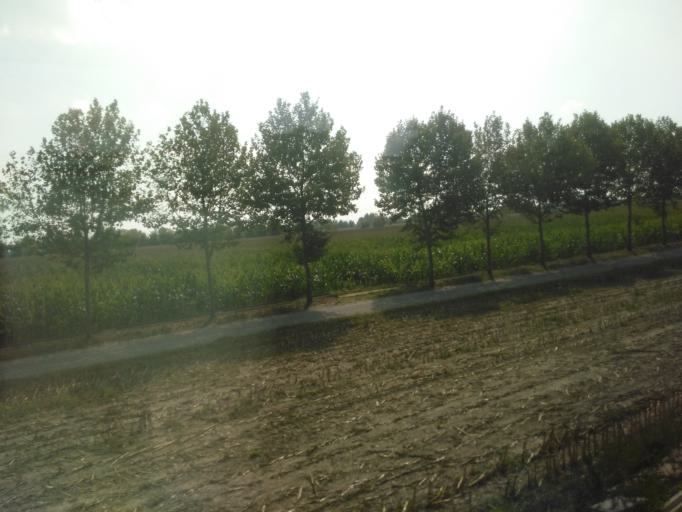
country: IT
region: Lombardy
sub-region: Provincia di Bergamo
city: Cortenuova
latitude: 45.5255
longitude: 9.7910
